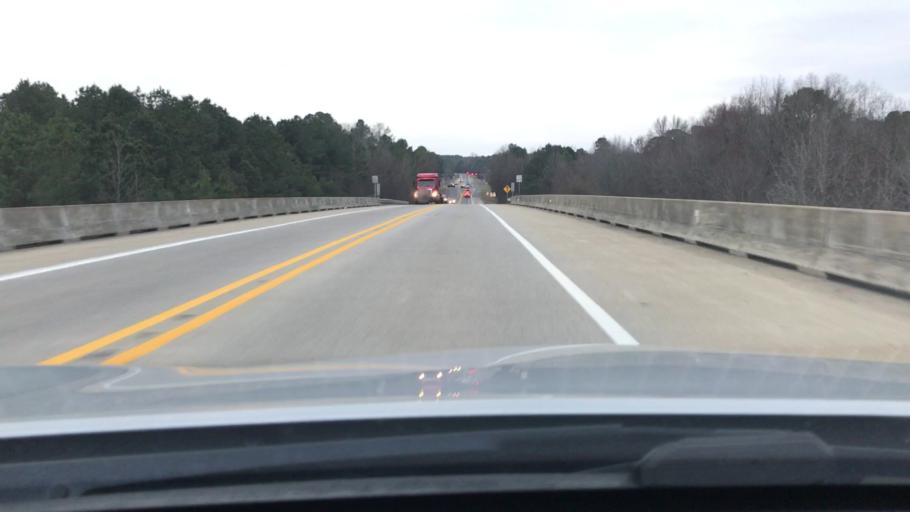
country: US
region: Arkansas
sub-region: Hempstead County
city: Hope
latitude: 33.6723
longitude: -93.5758
